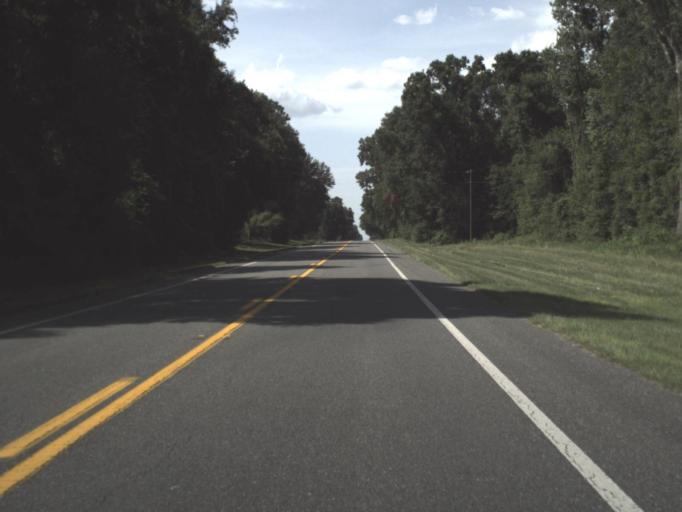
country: US
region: Florida
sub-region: Alachua County
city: High Springs
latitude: 29.9789
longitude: -82.7099
